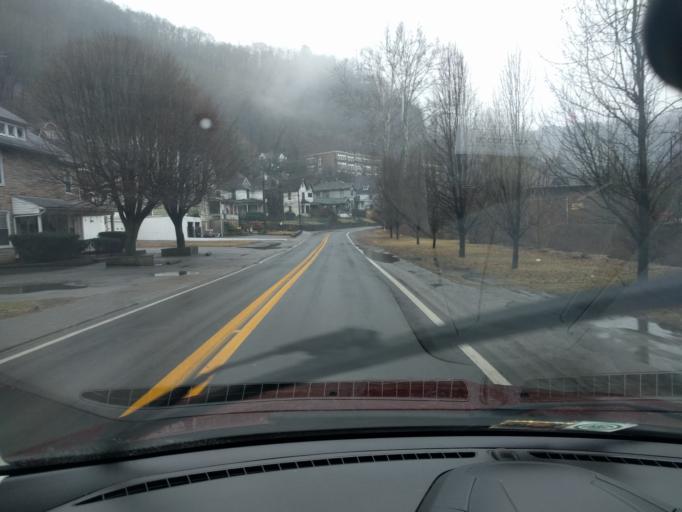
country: US
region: West Virginia
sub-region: McDowell County
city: Welch
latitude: 37.4339
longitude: -81.5817
